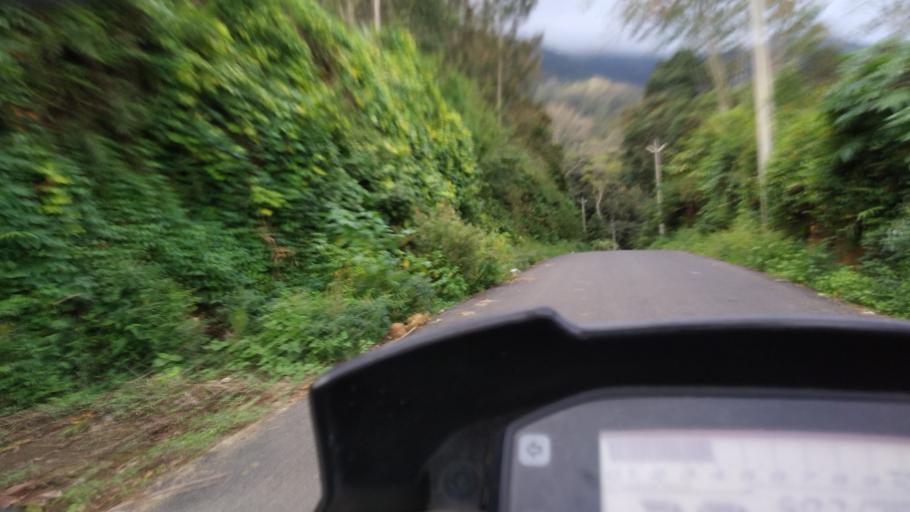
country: IN
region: Tamil Nadu
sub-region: Theni
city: Bodinayakkanur
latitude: 10.0342
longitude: 77.2291
